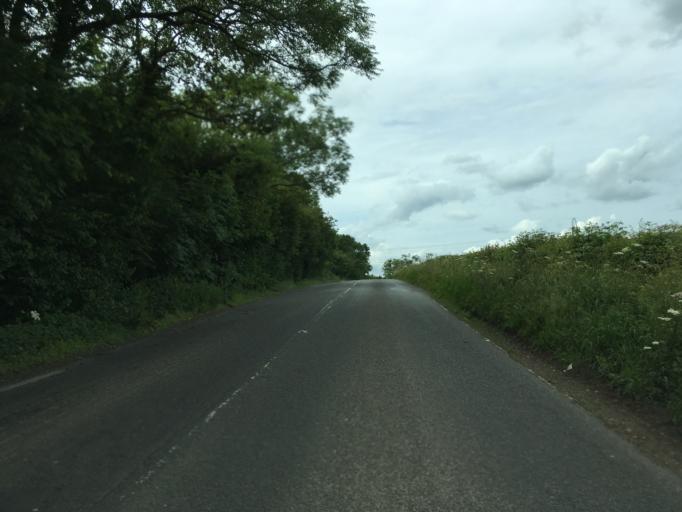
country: GB
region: England
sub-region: Wiltshire
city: Charlton
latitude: 51.5654
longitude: -2.0165
